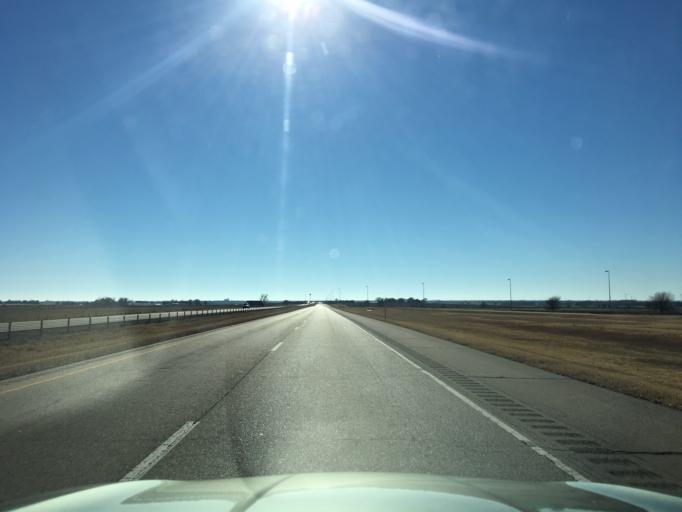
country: US
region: Oklahoma
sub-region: Kay County
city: Blackwell
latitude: 36.9830
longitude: -97.3458
